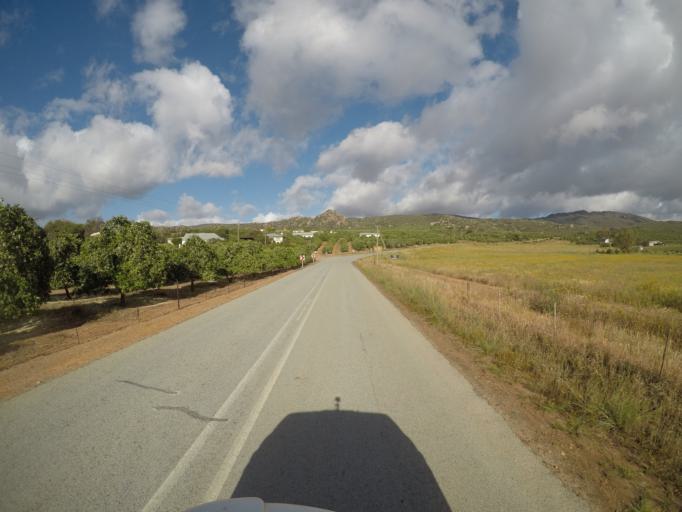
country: ZA
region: Western Cape
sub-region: West Coast District Municipality
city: Clanwilliam
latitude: -32.4381
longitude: 18.9433
